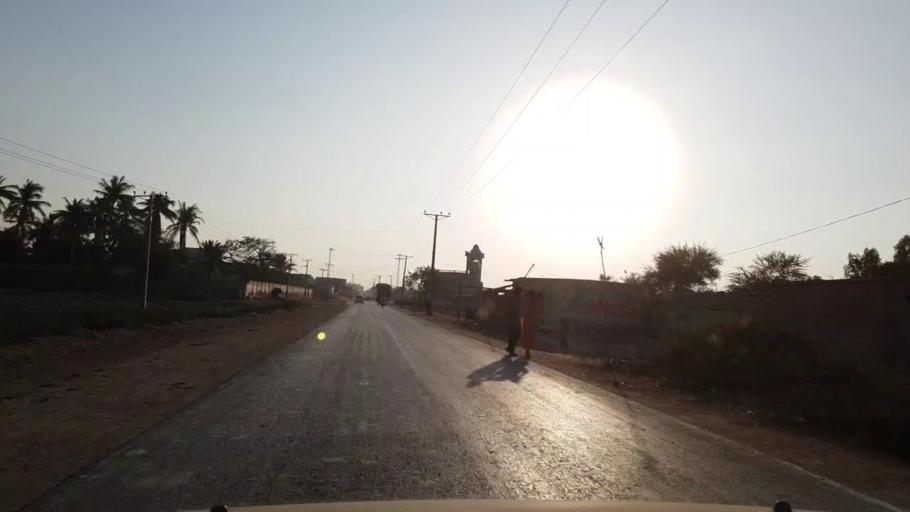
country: PK
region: Sindh
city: Daro Mehar
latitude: 24.6095
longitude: 68.0852
